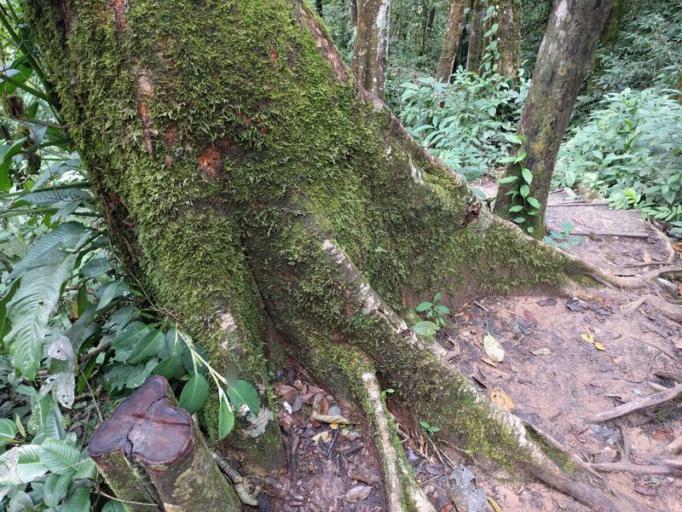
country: BO
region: Cochabamba
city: Chimore
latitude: -16.9667
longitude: -65.4116
